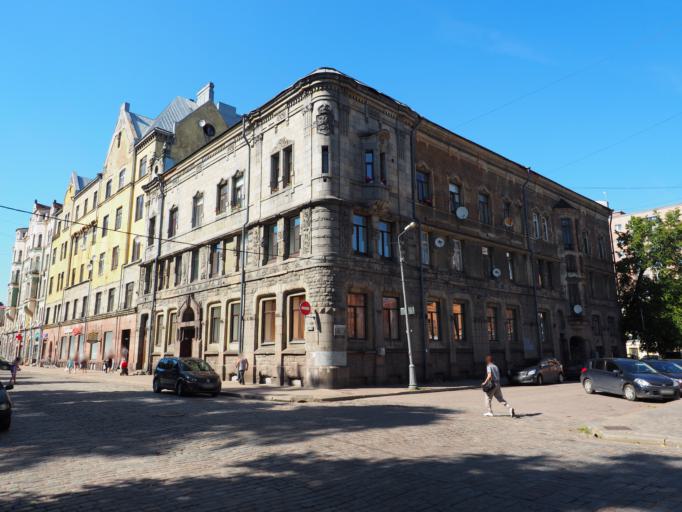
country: RU
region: Leningrad
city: Vyborg
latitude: 60.7119
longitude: 28.7428
